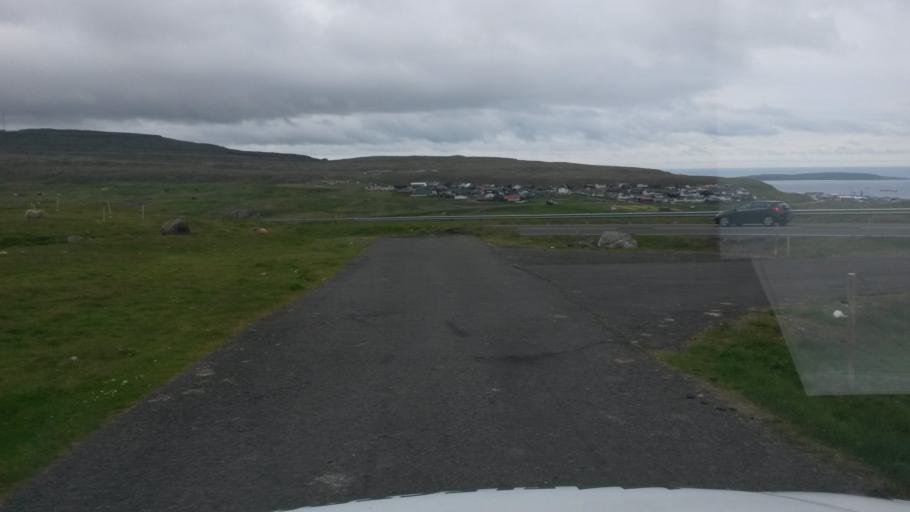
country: FO
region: Streymoy
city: Argir
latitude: 61.9956
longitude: -6.8449
